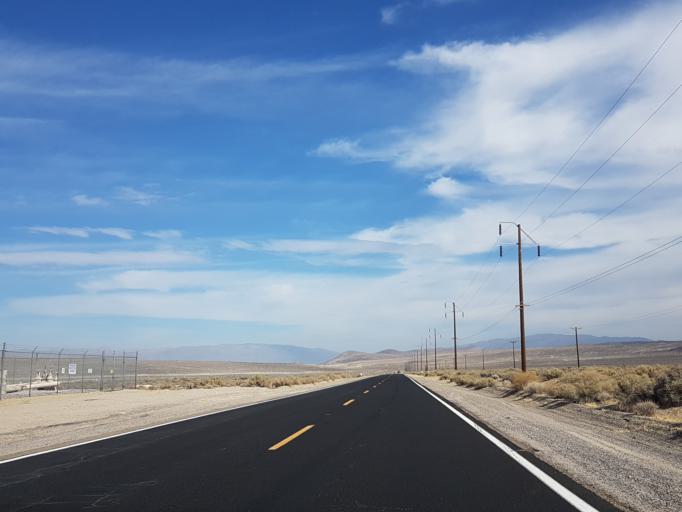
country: US
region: California
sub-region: San Bernardino County
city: Searles Valley
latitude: 35.6476
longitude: -117.5039
